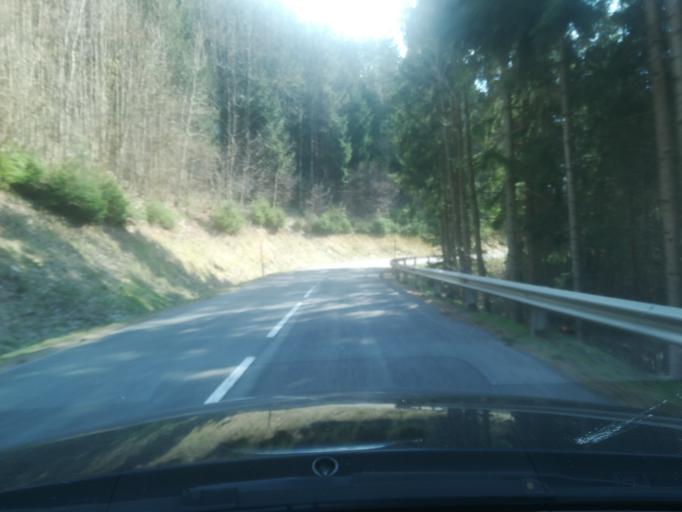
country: AT
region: Upper Austria
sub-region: Politischer Bezirk Freistadt
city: Freistadt
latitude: 48.4446
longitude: 14.6488
